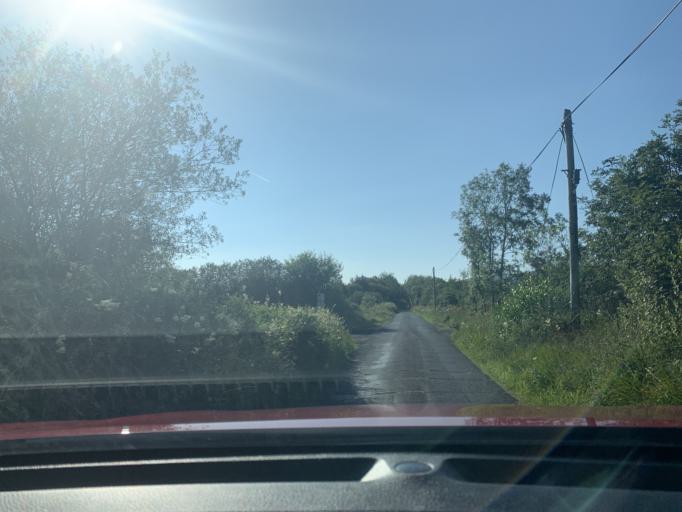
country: IE
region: Connaught
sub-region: Sligo
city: Tobercurry
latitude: 54.0778
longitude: -8.7994
